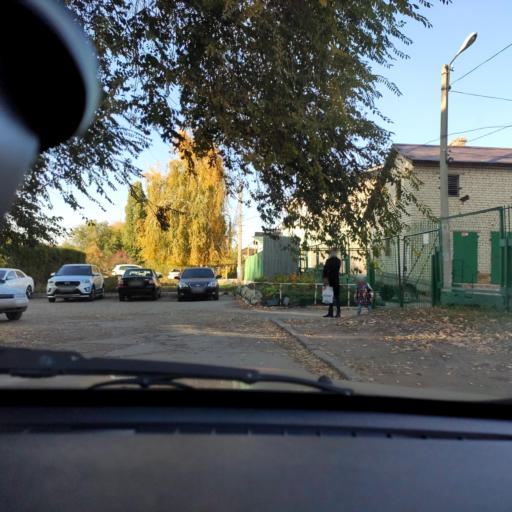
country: RU
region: Samara
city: Tol'yatti
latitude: 53.5303
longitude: 49.4061
